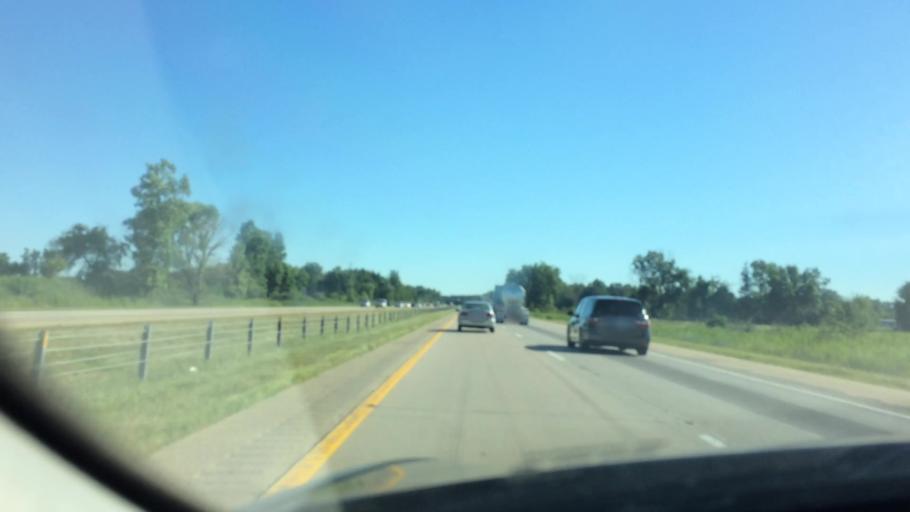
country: US
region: Michigan
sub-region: Monroe County
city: Petersburg
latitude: 41.8389
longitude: -83.6727
